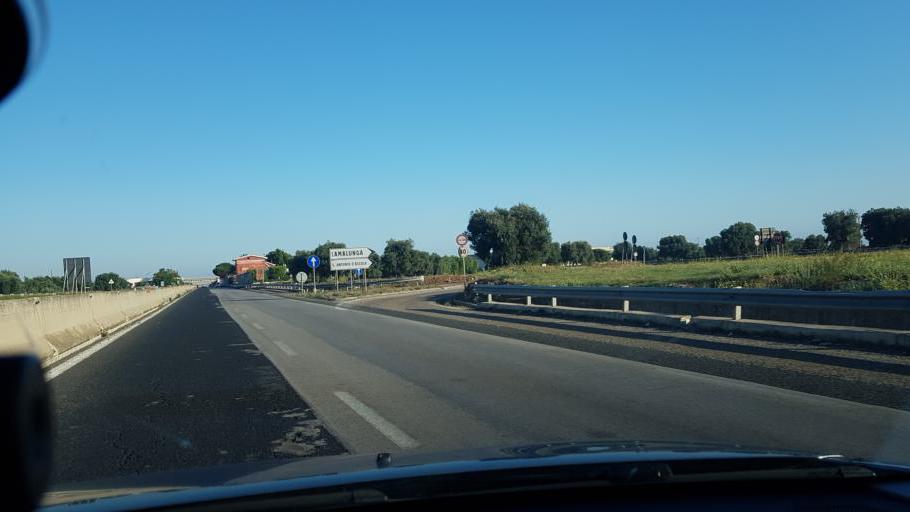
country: IT
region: Apulia
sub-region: Provincia di Brindisi
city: Fasano
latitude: 40.8742
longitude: 17.3416
